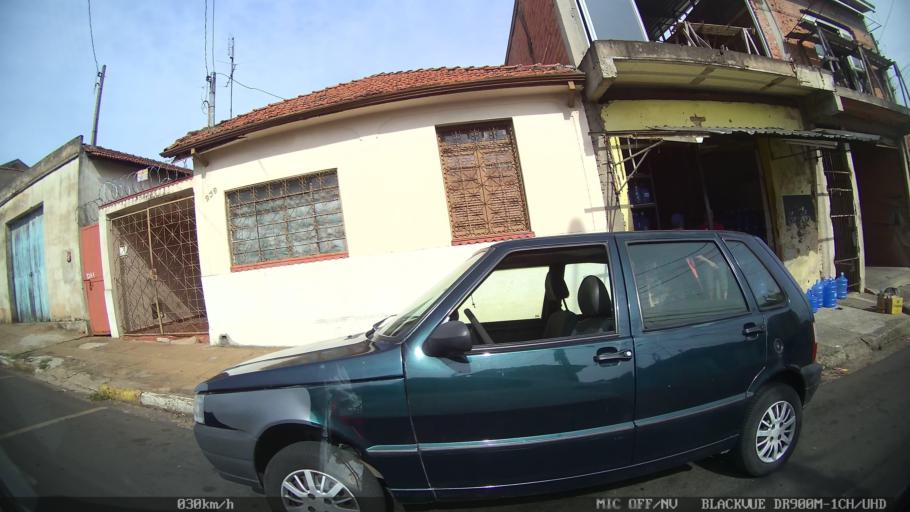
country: BR
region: Sao Paulo
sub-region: Piracicaba
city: Piracicaba
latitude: -22.7396
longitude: -47.6610
